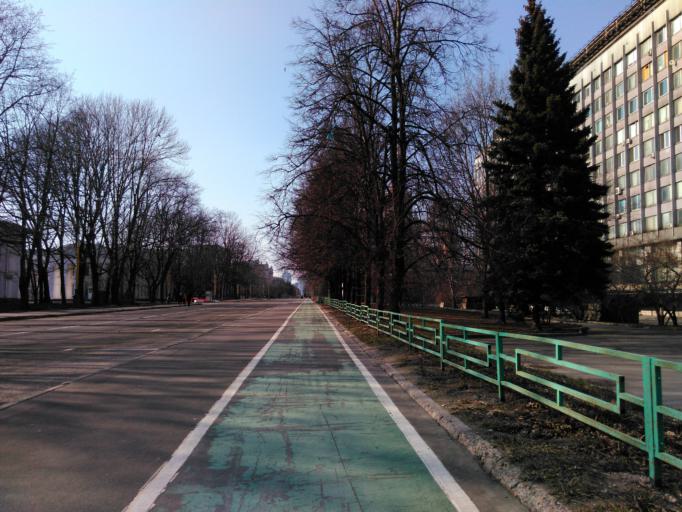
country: RU
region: Moskovskaya
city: Semenovskoye
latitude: 55.6971
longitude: 37.5383
